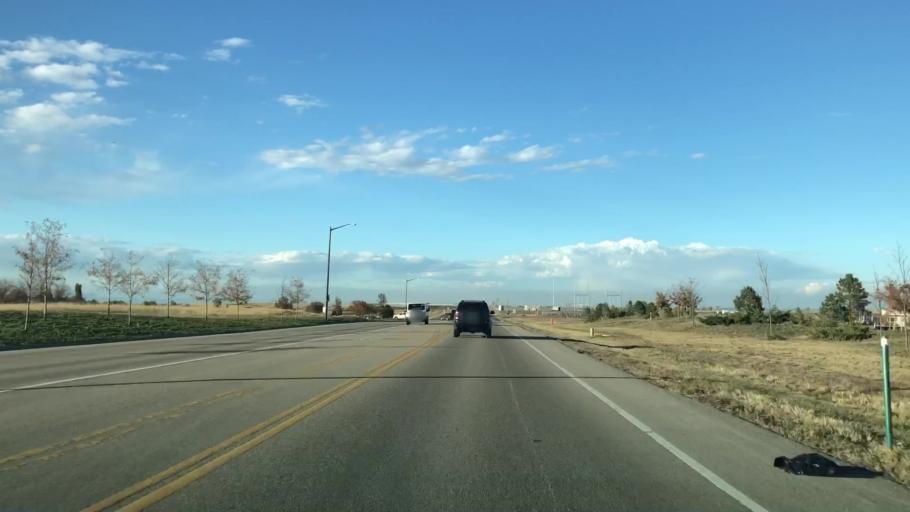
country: US
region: Colorado
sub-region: Larimer County
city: Loveland
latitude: 40.4414
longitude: -105.0204
